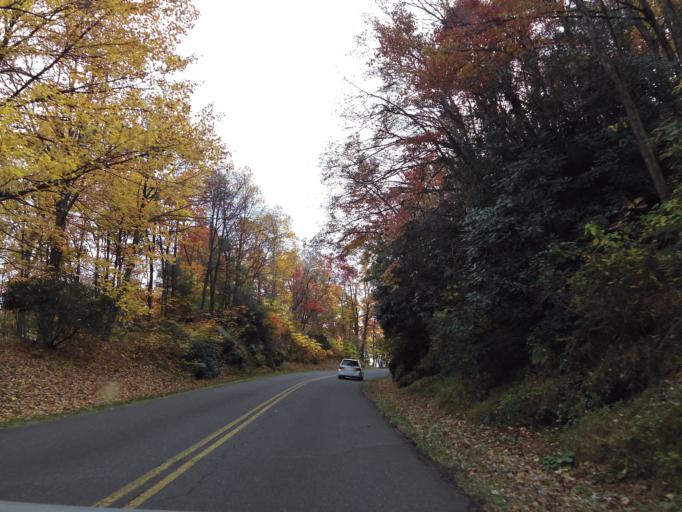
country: US
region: North Carolina
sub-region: Ashe County
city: Jefferson
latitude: 36.2970
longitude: -81.3667
